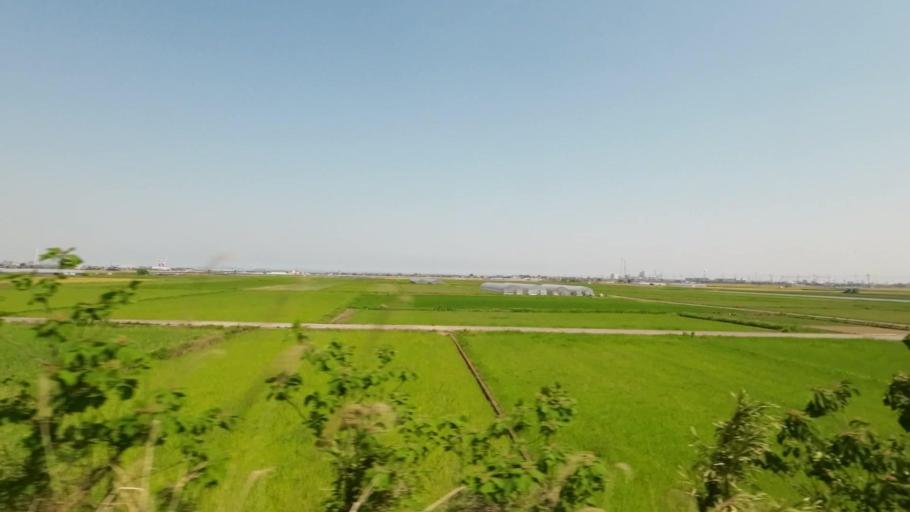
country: JP
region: Ehime
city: Saijo
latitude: 33.8959
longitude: 133.1529
